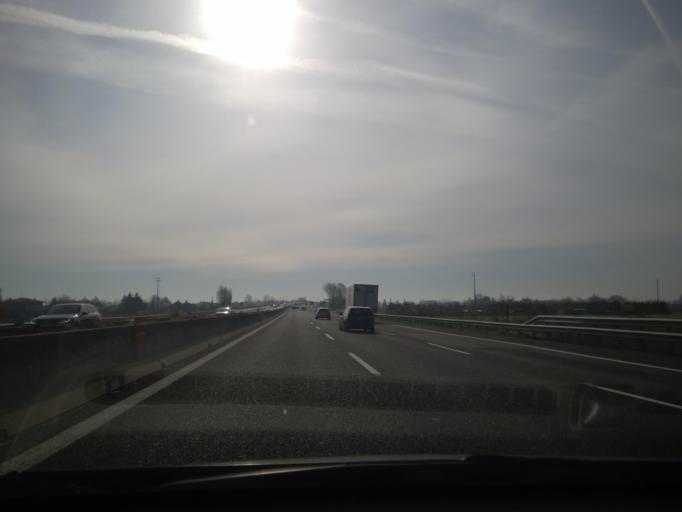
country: IT
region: Emilia-Romagna
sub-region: Provincia di Ravenna
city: Solarolo
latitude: 44.3486
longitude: 11.8324
